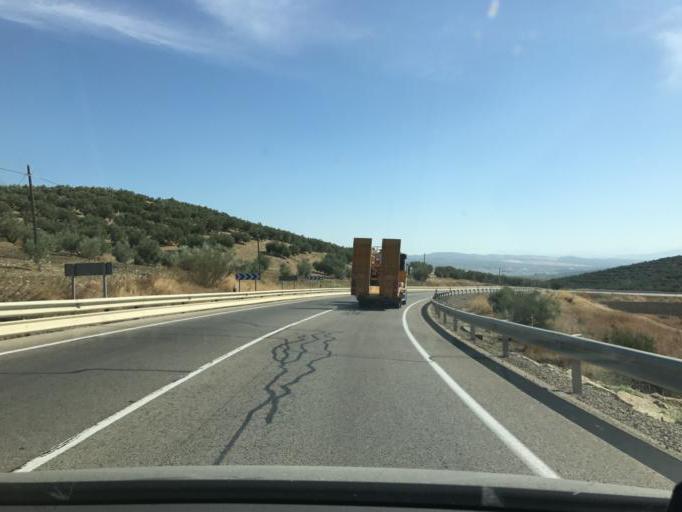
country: ES
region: Andalusia
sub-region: Province of Cordoba
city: Espejo
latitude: 37.6873
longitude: -4.5314
